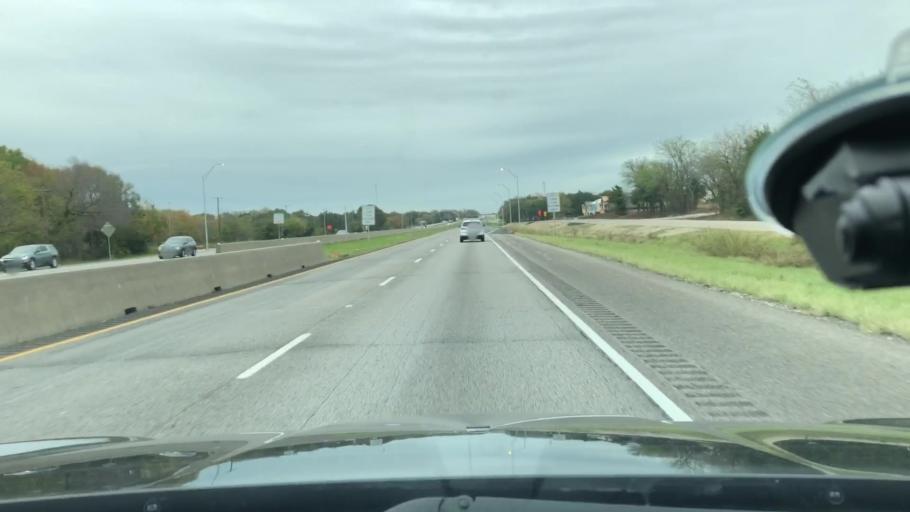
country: US
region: Texas
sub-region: Hunt County
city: Commerce
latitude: 33.1305
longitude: -95.8226
